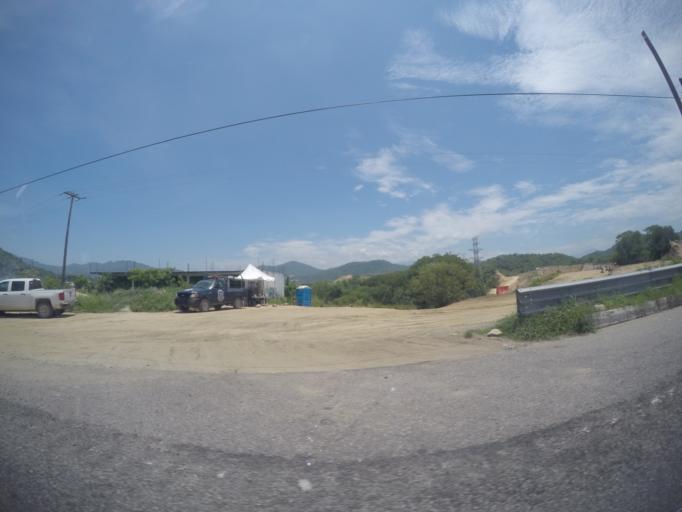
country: MX
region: Guerrero
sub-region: Acapulco de Juarez
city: Colonia Nueva Revolucion
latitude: 16.9255
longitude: -99.8079
